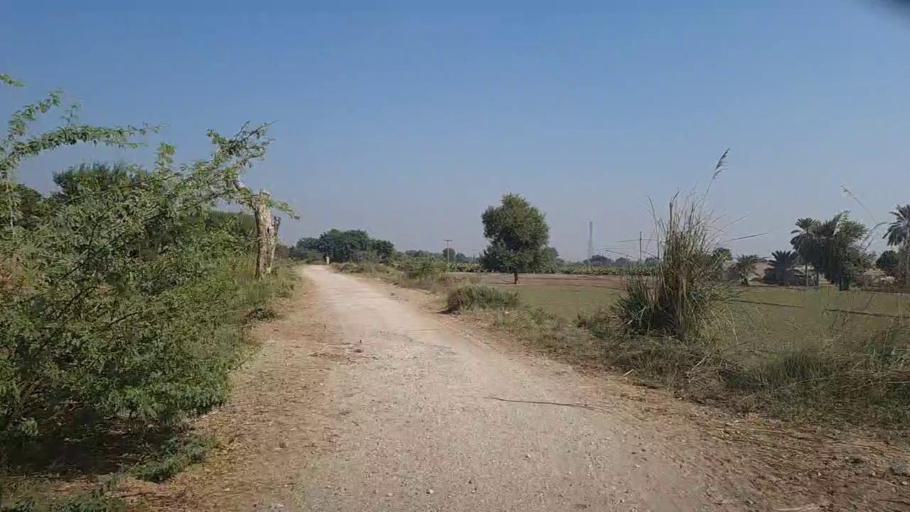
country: PK
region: Sindh
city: Bozdar
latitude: 27.1938
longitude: 68.6353
